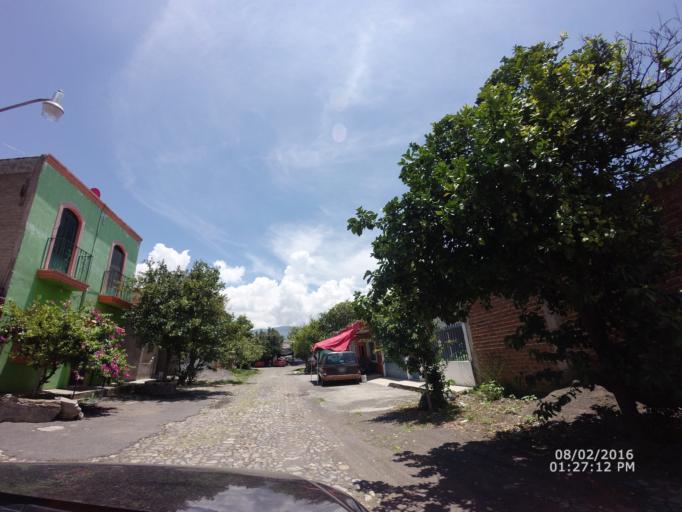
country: MX
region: Nayarit
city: Ixtlan del Rio
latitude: 21.0399
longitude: -104.3774
